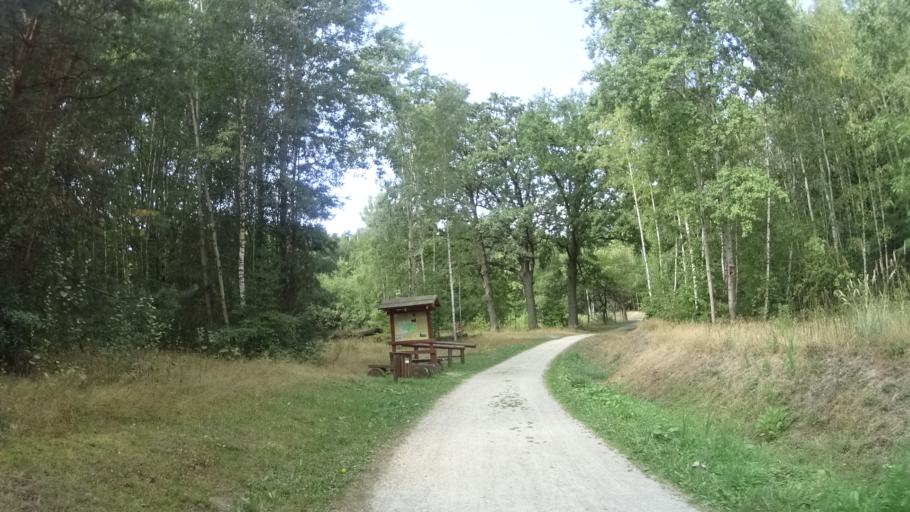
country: PL
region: Lubusz
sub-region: Powiat zarski
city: Leknica
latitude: 51.5355
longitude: 14.7558
